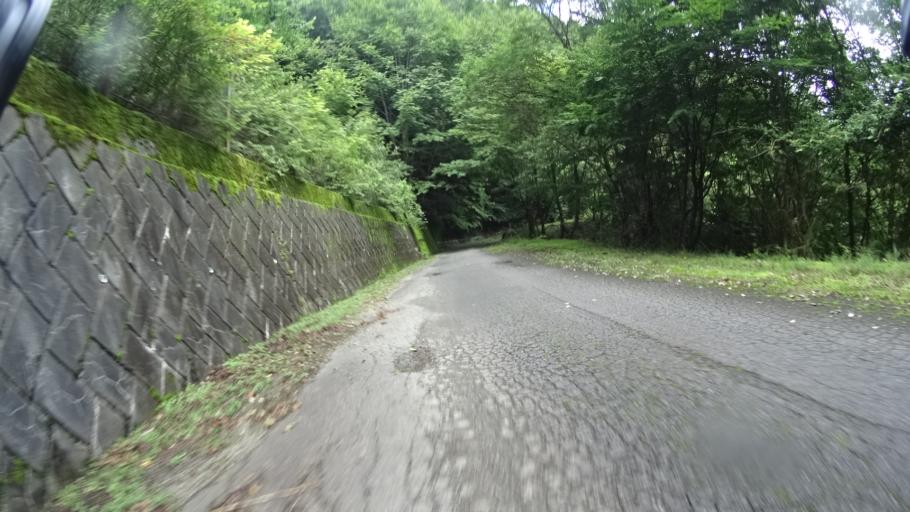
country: JP
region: Saitama
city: Chichibu
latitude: 35.8941
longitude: 139.1237
